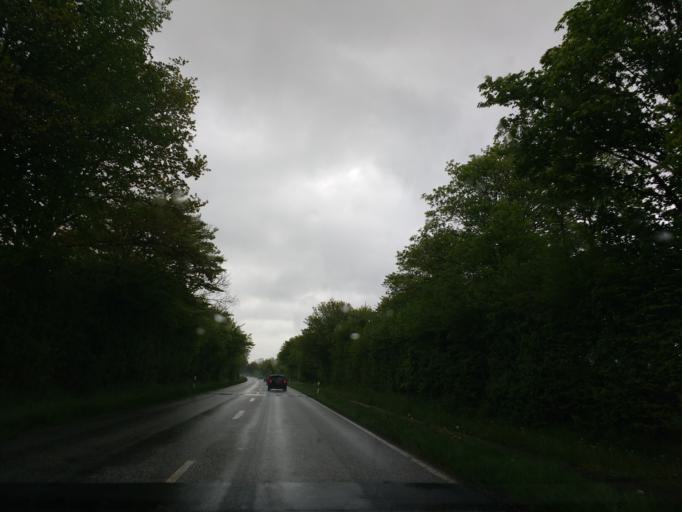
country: DE
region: Schleswig-Holstein
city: Loose
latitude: 54.5103
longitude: 9.8660
